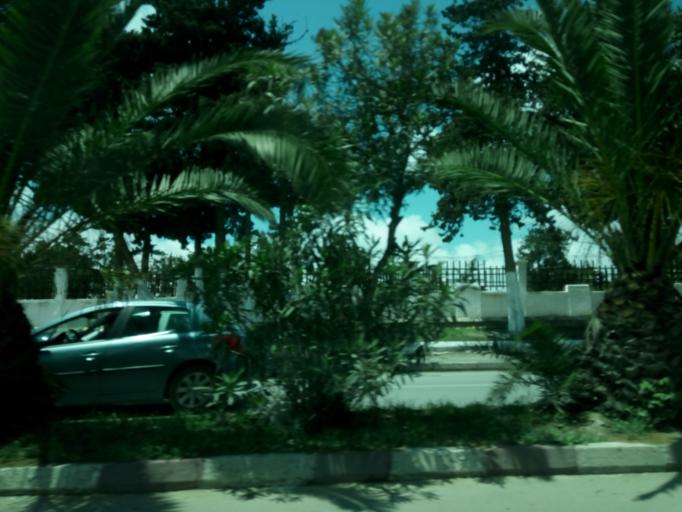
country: DZ
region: Tipaza
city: Saoula
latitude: 36.7291
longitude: 2.9918
